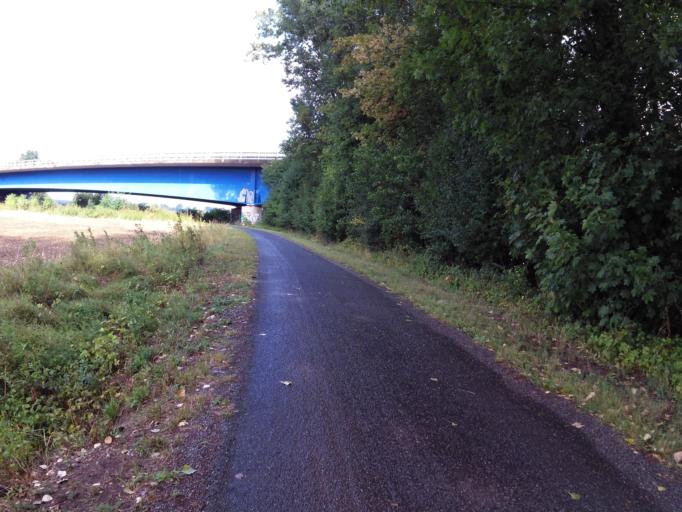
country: DE
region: Lower Saxony
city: Nienburg
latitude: 52.6572
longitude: 9.1990
